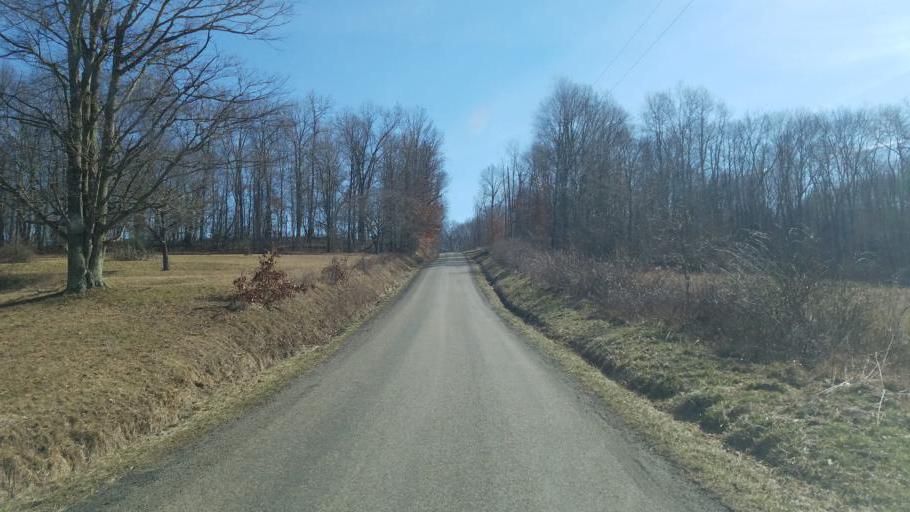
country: US
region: Ohio
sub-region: Ashland County
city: Loudonville
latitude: 40.5754
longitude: -82.3199
